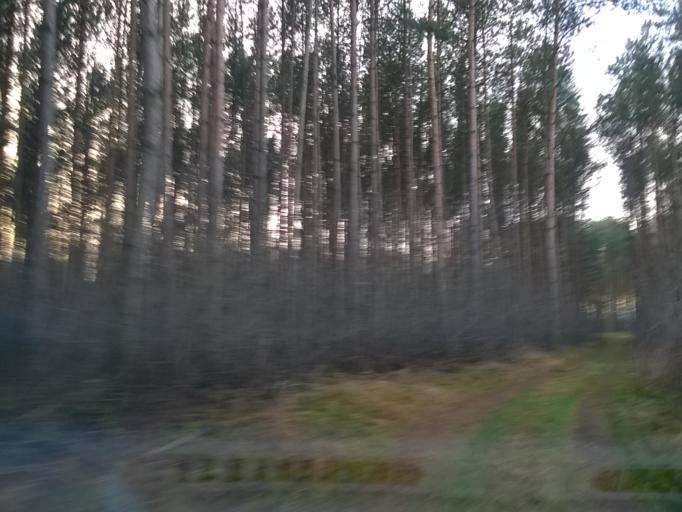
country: PL
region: Kujawsko-Pomorskie
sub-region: Powiat nakielski
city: Kcynia
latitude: 53.0277
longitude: 17.4418
